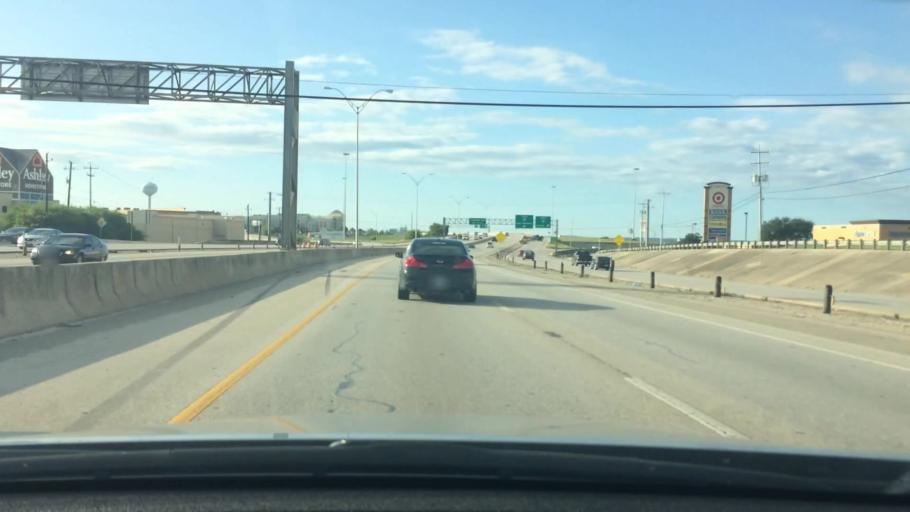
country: US
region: Texas
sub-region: Bexar County
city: Live Oak
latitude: 29.5642
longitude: -98.3298
